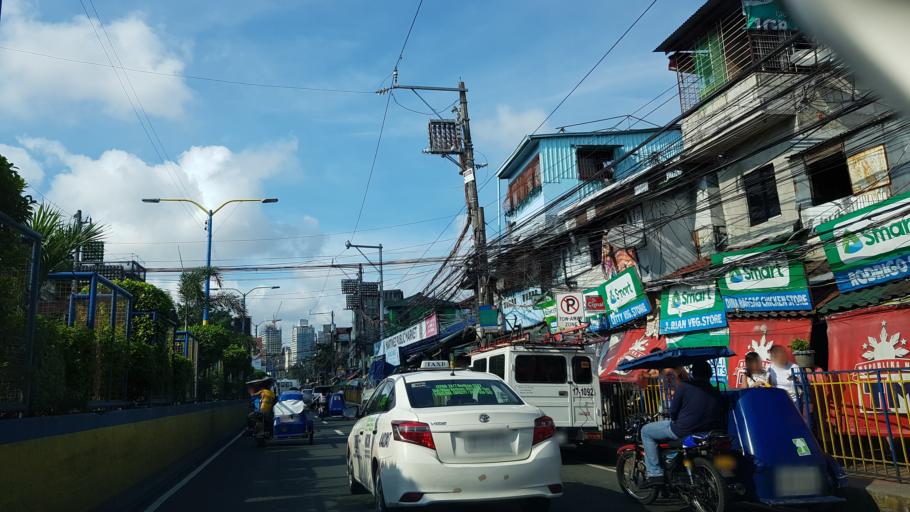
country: PH
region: Metro Manila
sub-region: Mandaluyong
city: Mandaluyong City
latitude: 14.5806
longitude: 121.0364
